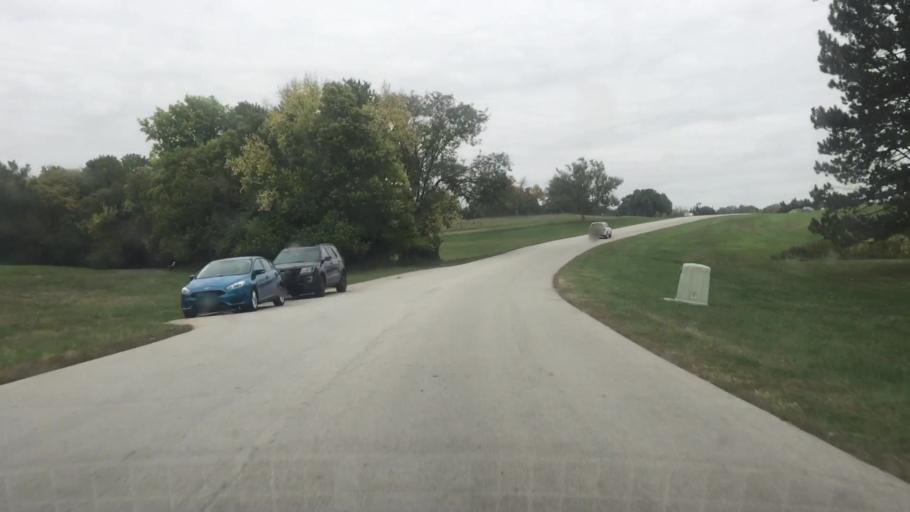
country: US
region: Kansas
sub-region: Johnson County
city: Lenexa
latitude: 38.9889
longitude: -94.7969
